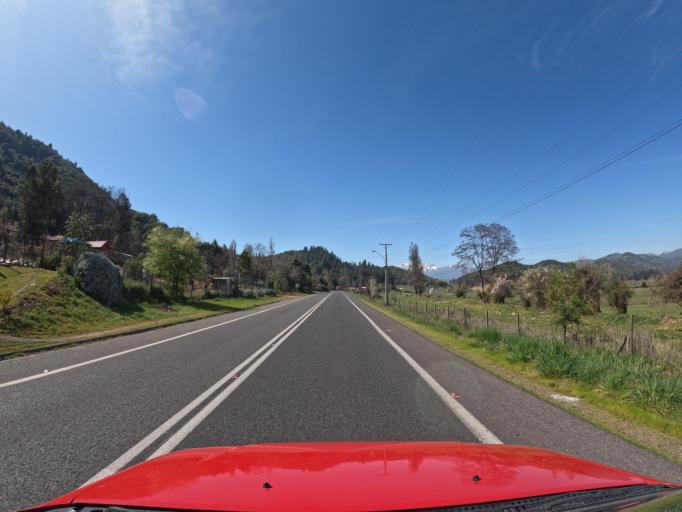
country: CL
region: Maule
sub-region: Provincia de Curico
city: Teno
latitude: -34.9791
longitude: -70.9793
